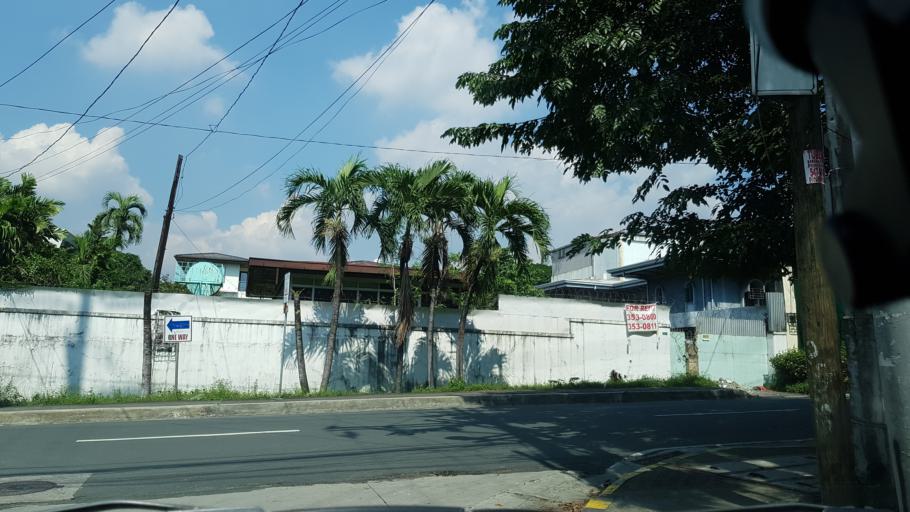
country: PH
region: Metro Manila
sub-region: San Juan
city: San Juan
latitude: 14.6164
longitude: 121.0359
